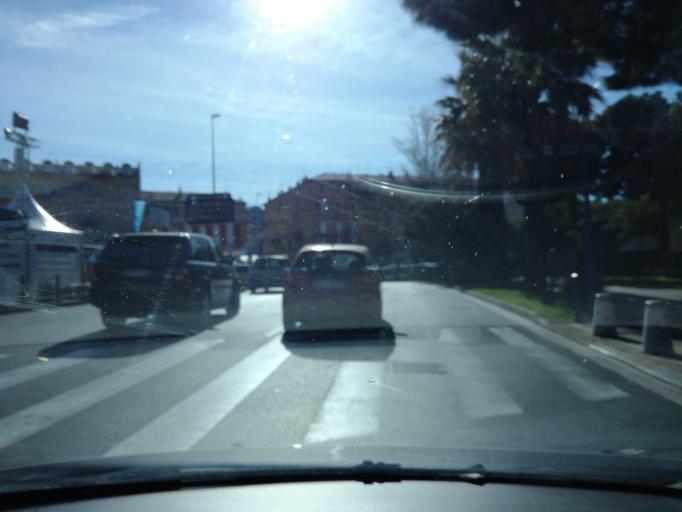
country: FR
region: Provence-Alpes-Cote d'Azur
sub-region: Departement des Alpes-Maritimes
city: Nice
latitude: 43.7067
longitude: 7.2814
